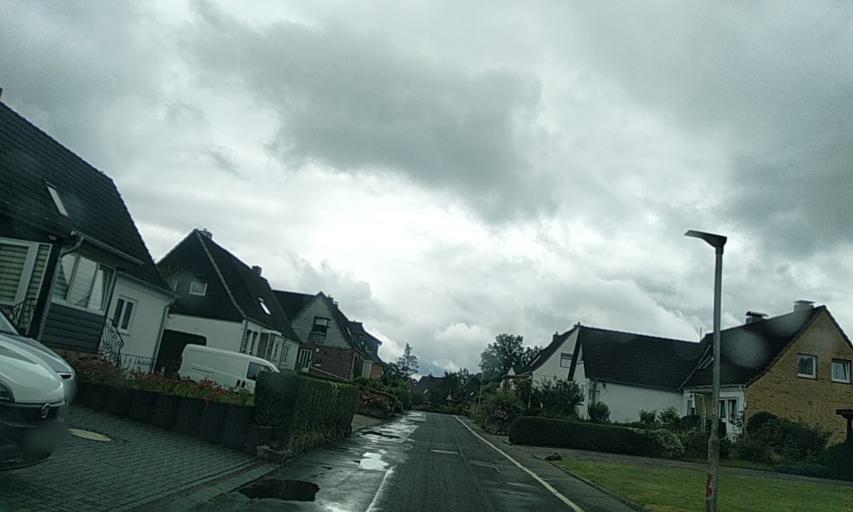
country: DE
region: Schleswig-Holstein
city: Schleswig
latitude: 54.5276
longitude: 9.5469
